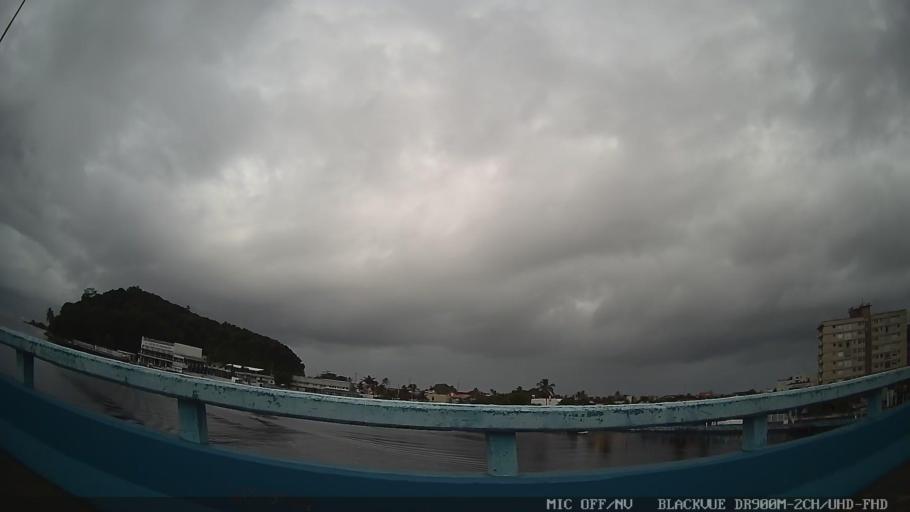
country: BR
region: Sao Paulo
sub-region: Itanhaem
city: Itanhaem
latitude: -24.1897
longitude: -46.7960
